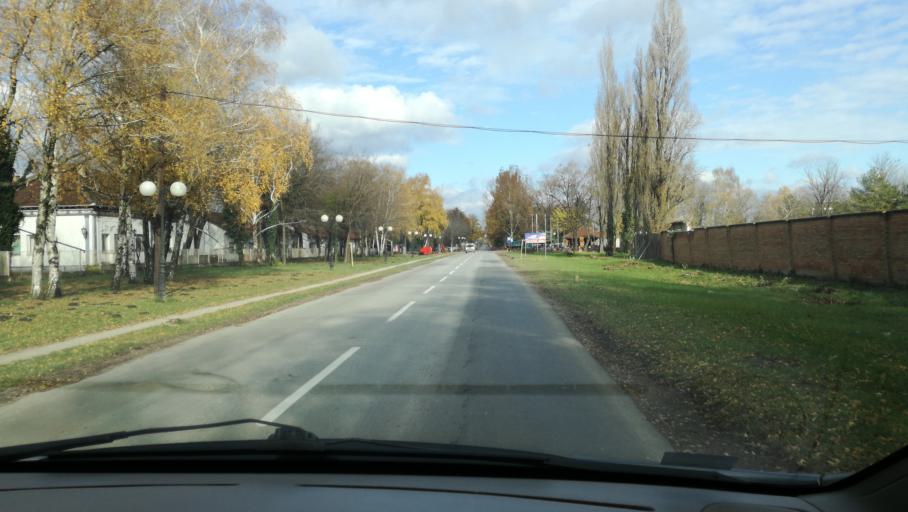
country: RS
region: Autonomna Pokrajina Vojvodina
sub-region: Severnobanatski Okrug
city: Kikinda
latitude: 45.8085
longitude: 20.4462
